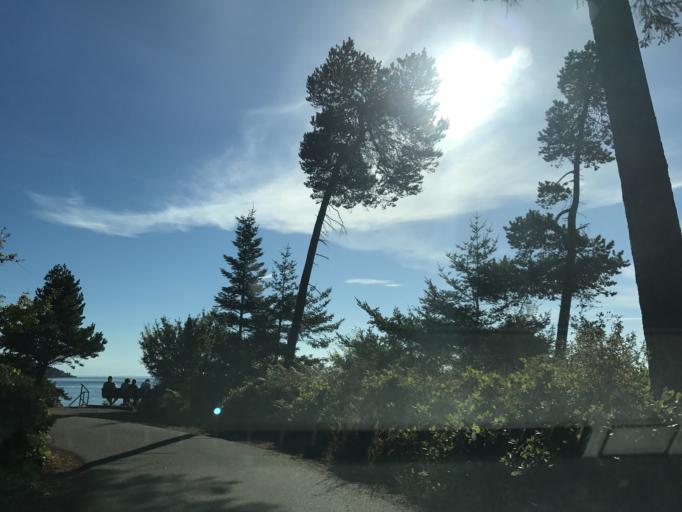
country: US
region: Washington
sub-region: Skagit County
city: Anacortes
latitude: 48.4982
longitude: -122.7010
